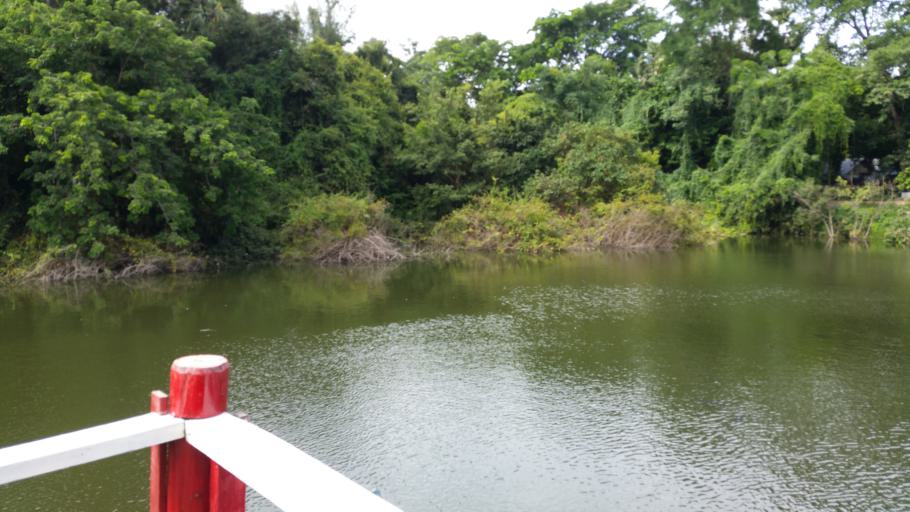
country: MM
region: Magway
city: Chauk
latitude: 21.1273
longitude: 94.8520
